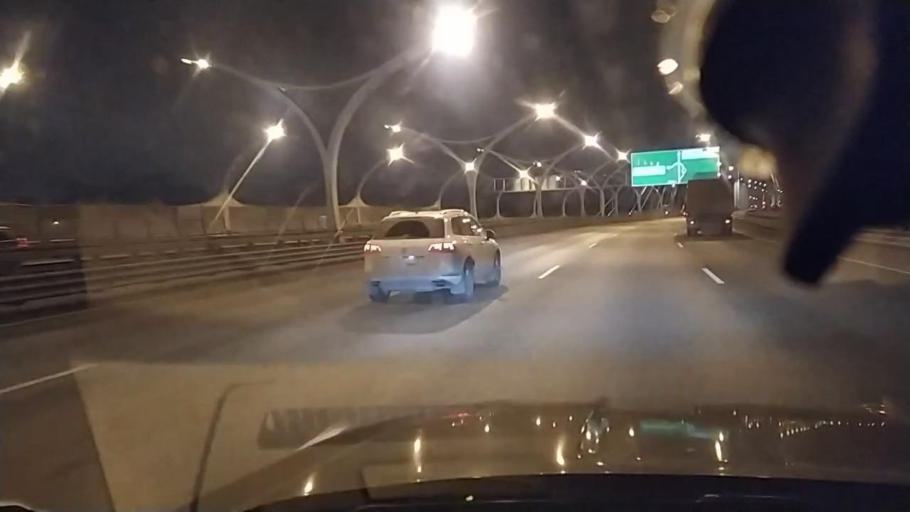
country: RU
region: St.-Petersburg
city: Staraya Derevnya
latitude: 59.9703
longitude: 30.2152
